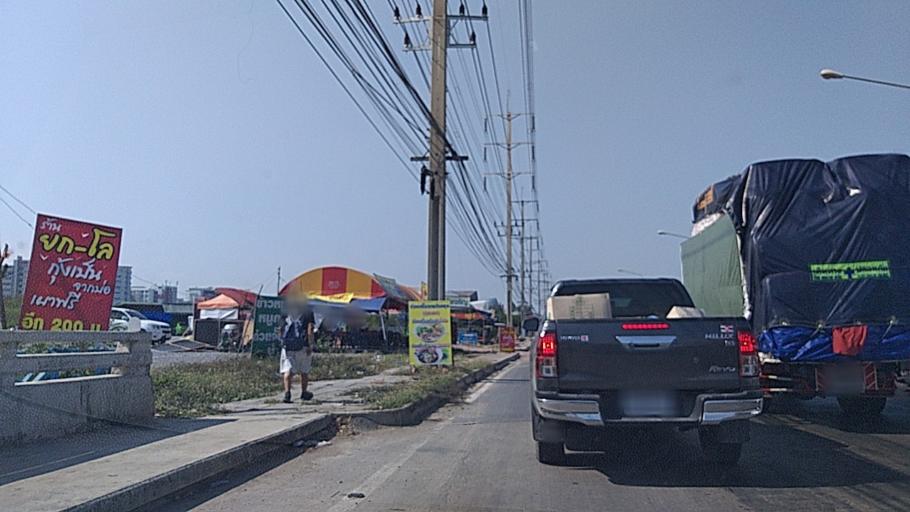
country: TH
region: Nakhon Pathom
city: Salaya
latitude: 13.7913
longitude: 100.3029
